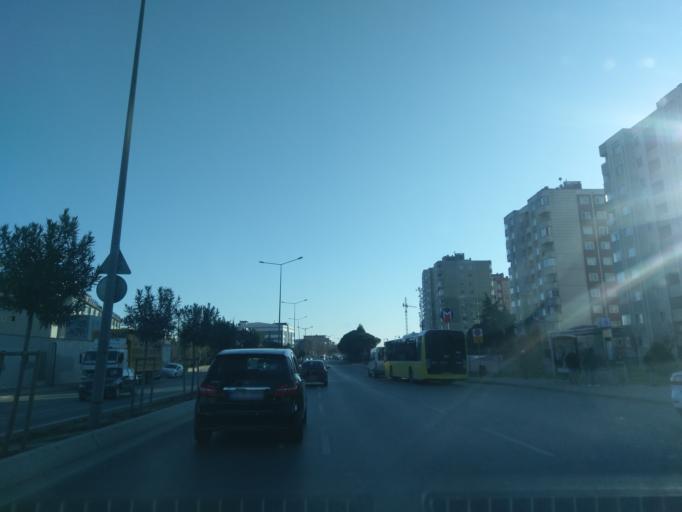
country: TR
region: Istanbul
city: Basaksehir
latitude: 41.0976
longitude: 28.7912
